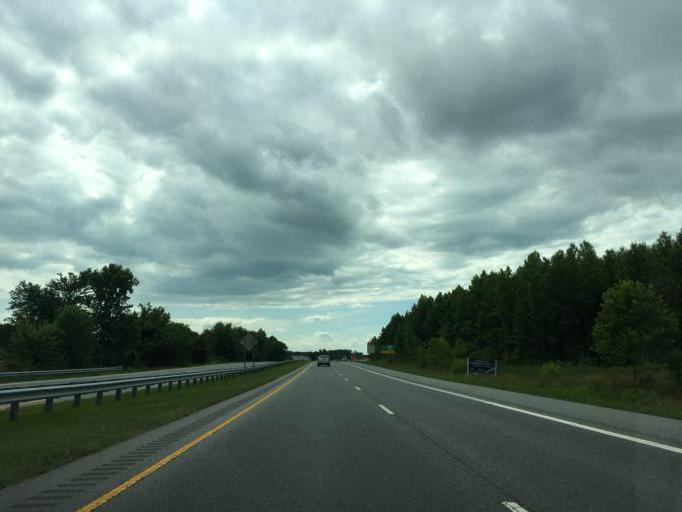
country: US
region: Maryland
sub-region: Caroline County
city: Ridgely
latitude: 38.9198
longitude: -75.9294
